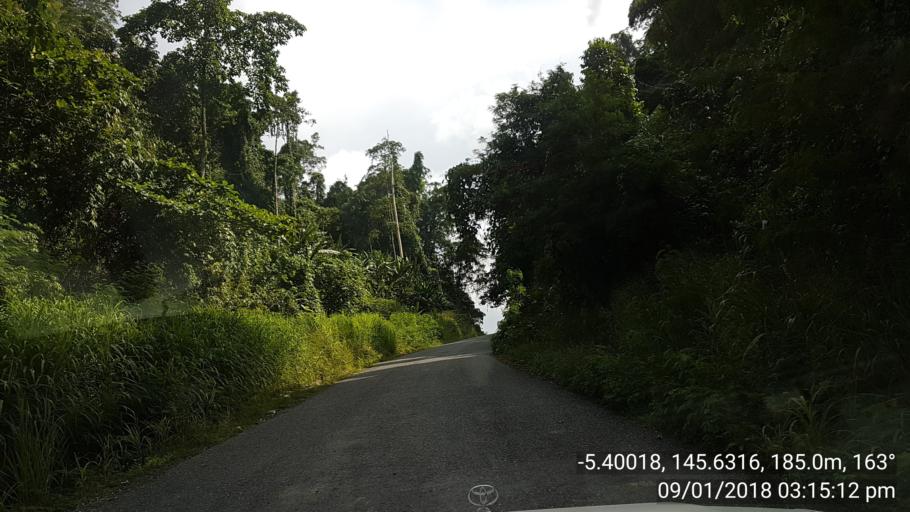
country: PG
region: Madang
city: Madang
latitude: -5.4003
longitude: 145.6317
